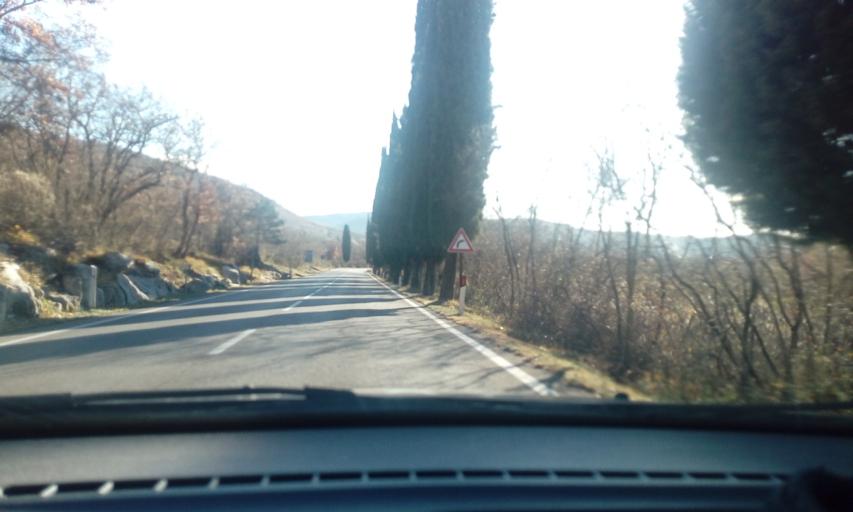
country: IT
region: Friuli Venezia Giulia
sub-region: Provincia di Gorizia
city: Doberdo del Lago
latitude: 45.8281
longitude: 13.5753
